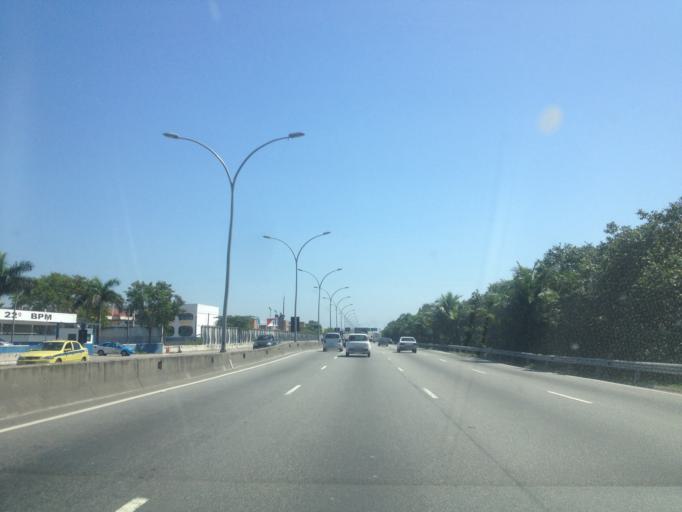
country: BR
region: Rio de Janeiro
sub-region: Rio De Janeiro
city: Rio de Janeiro
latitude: -22.8538
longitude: -43.2391
